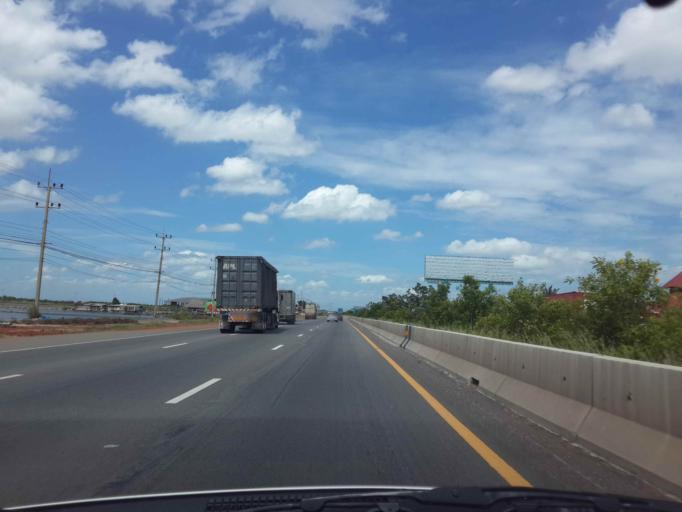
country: TH
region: Samut Songkhram
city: Samut Songkhram
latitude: 13.4409
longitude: 100.0654
